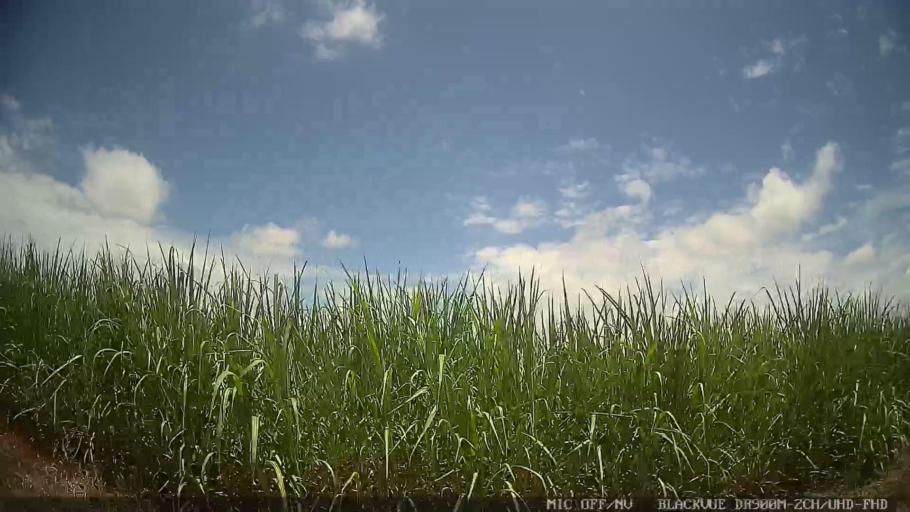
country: BR
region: Sao Paulo
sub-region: Laranjal Paulista
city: Laranjal Paulista
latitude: -23.0308
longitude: -47.8582
